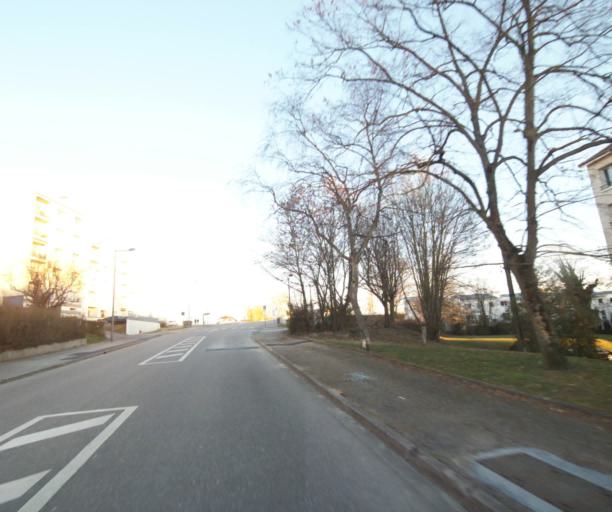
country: FR
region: Lorraine
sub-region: Departement de Meurthe-et-Moselle
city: Malzeville
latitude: 48.7051
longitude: 6.1934
